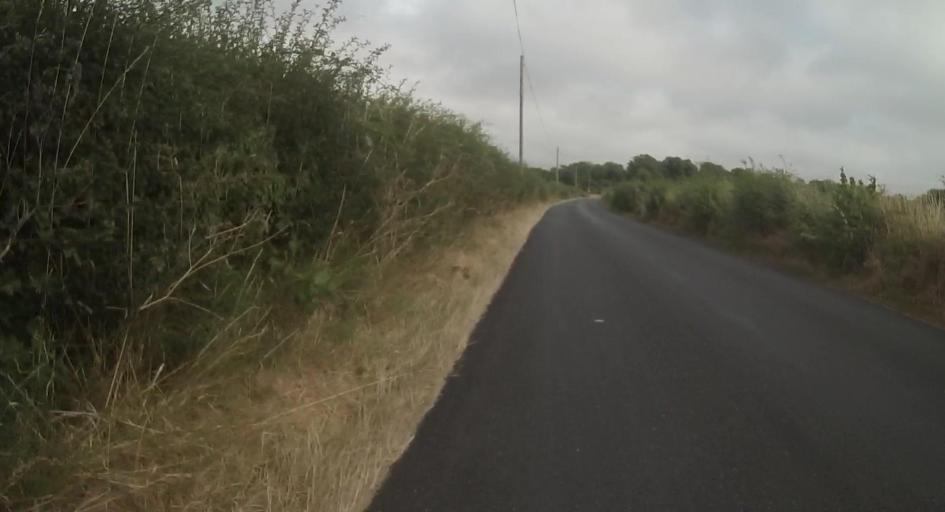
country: GB
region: England
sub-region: Dorset
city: Wool
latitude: 50.6815
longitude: -2.2144
